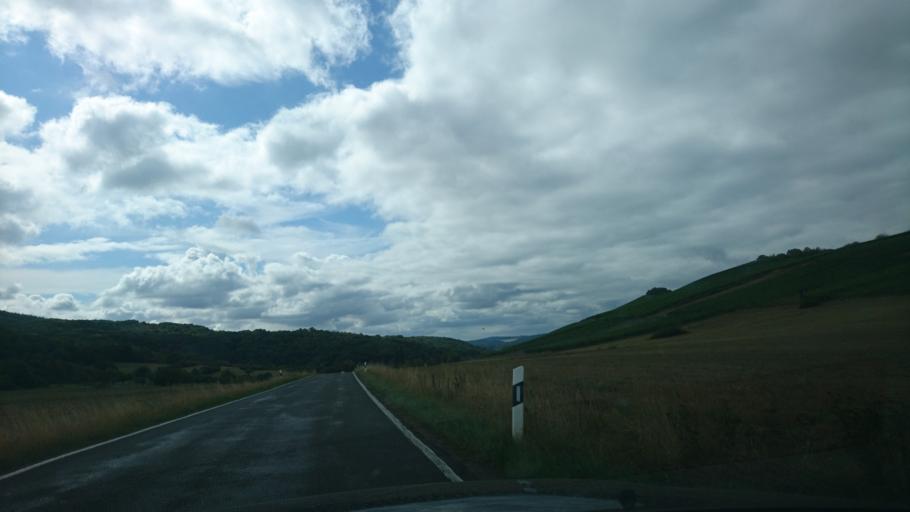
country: DE
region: Rheinland-Pfalz
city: Wiltingen
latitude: 49.6538
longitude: 6.6231
